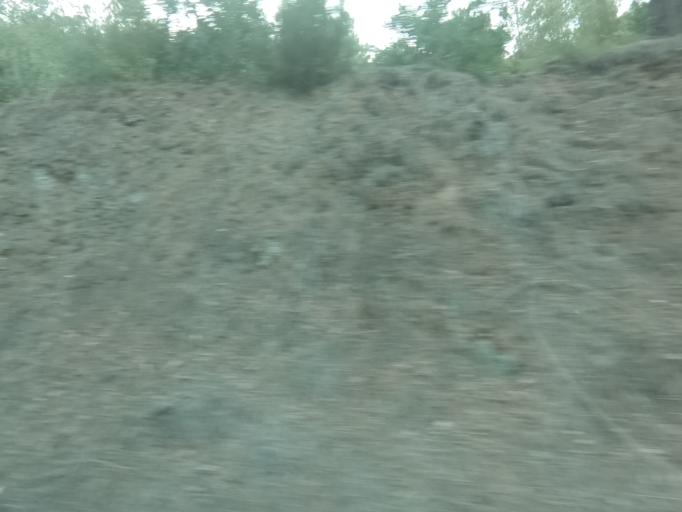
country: PT
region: Vila Real
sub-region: Sabrosa
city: Sabrosa
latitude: 41.2659
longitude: -7.5556
